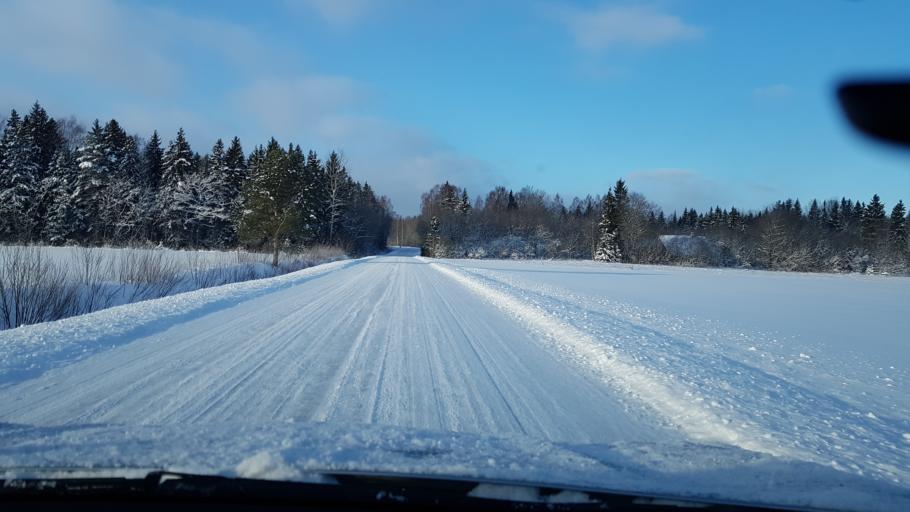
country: EE
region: Harju
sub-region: Nissi vald
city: Turba
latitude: 59.1029
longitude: 24.2453
